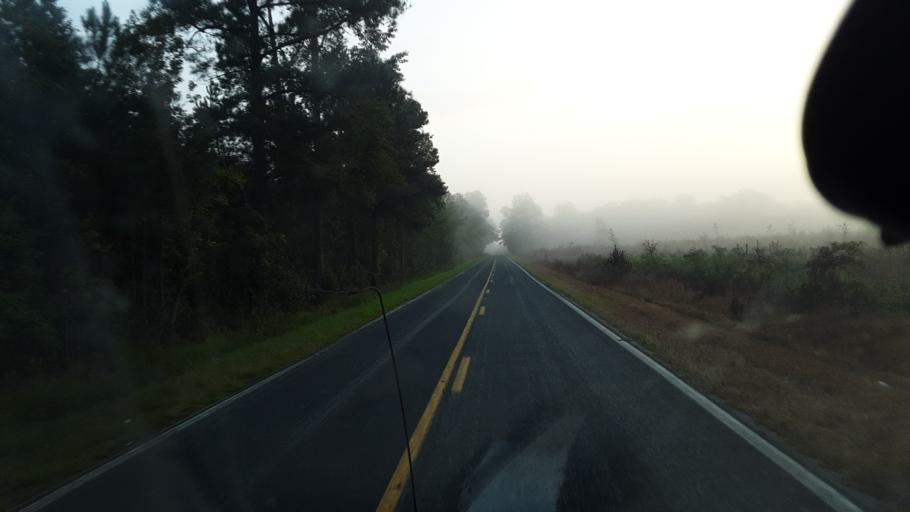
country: US
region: South Carolina
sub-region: Clarendon County
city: Manning
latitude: 33.7336
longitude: -80.0897
